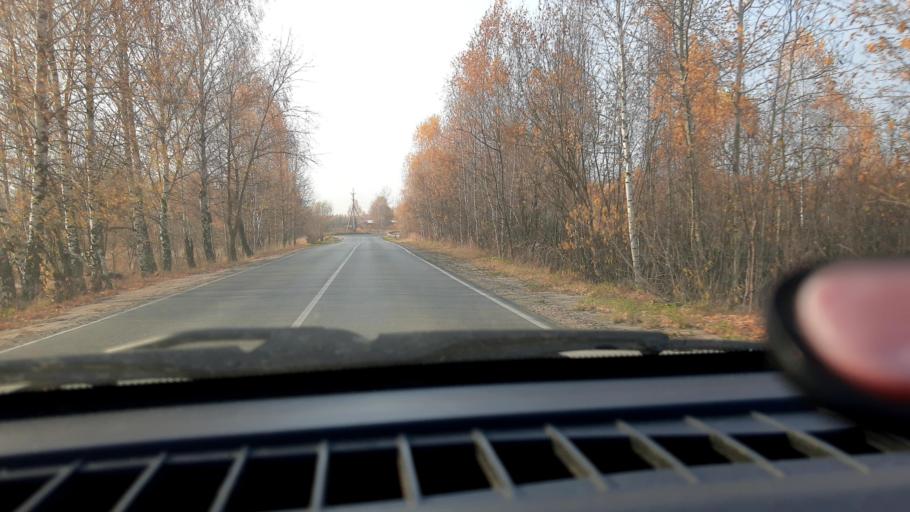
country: RU
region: Nizjnij Novgorod
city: Neklyudovo
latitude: 56.4756
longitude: 43.8783
